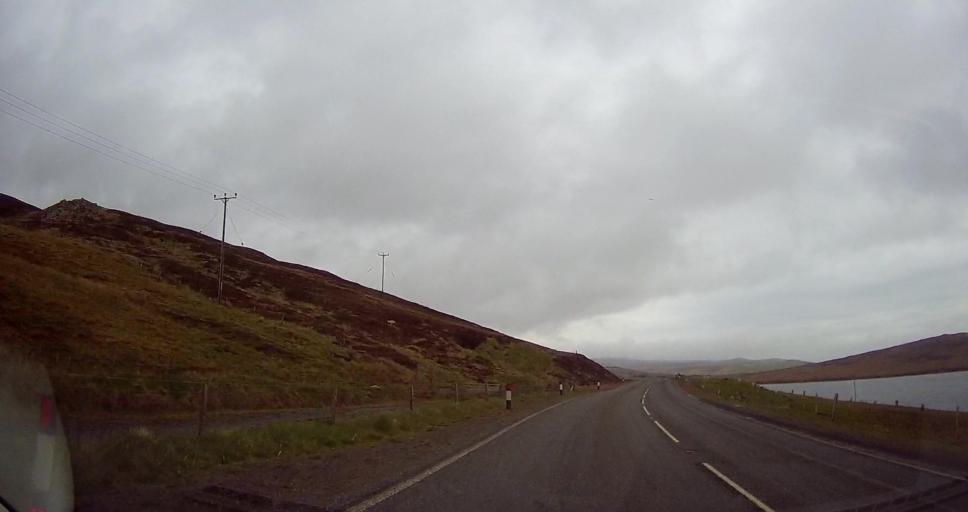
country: GB
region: Scotland
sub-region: Shetland Islands
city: Lerwick
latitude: 60.2564
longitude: -1.2263
